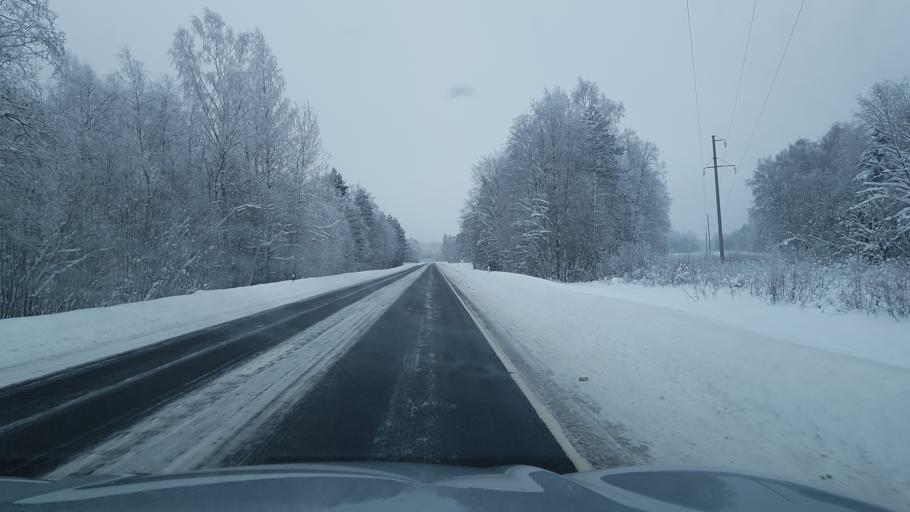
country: EE
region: Ida-Virumaa
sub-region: Johvi vald
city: Johvi
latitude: 59.2991
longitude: 27.3964
